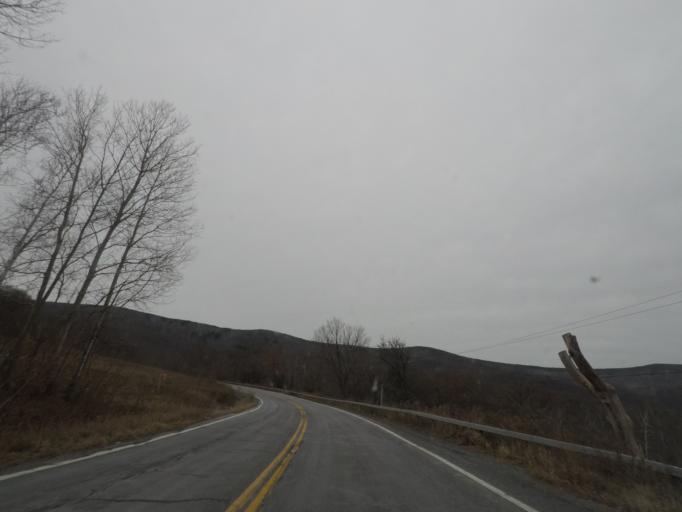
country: US
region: Massachusetts
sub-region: Berkshire County
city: Williamstown
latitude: 42.7404
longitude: -73.2982
